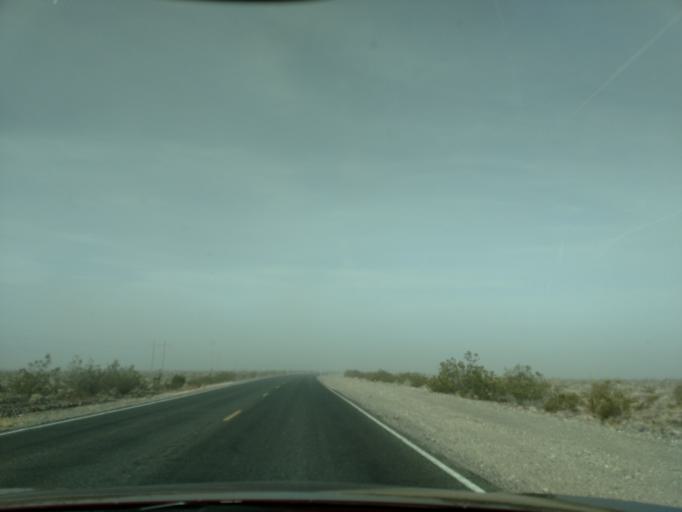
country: US
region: Nevada
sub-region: Nye County
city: Pahrump
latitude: 36.4434
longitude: -116.0971
